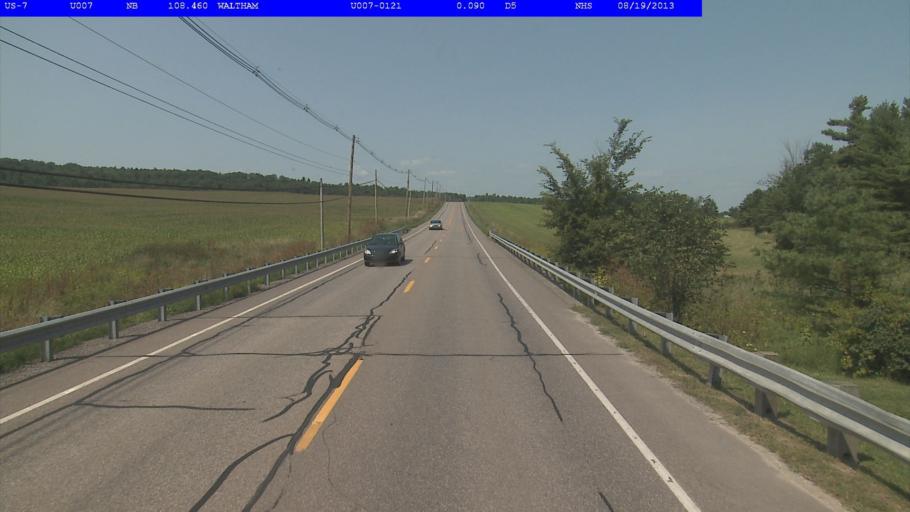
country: US
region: Vermont
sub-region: Addison County
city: Vergennes
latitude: 44.1486
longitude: -73.2114
